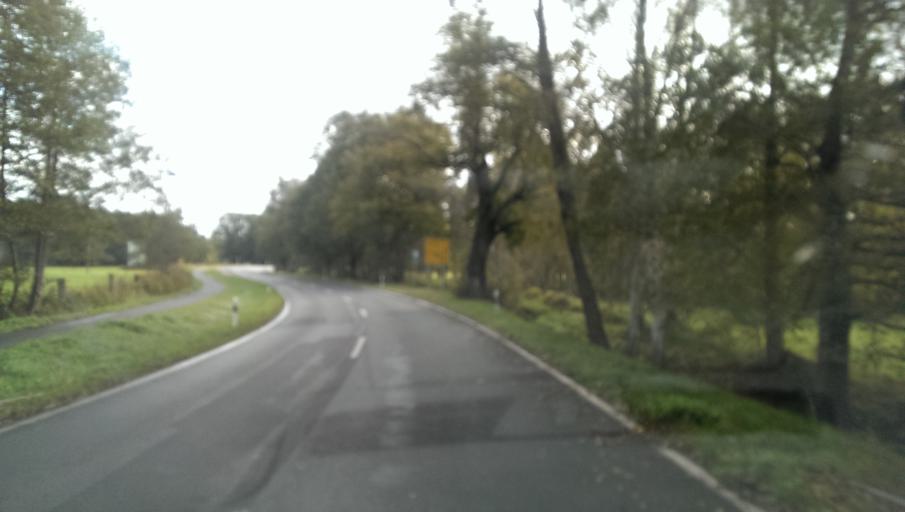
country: DE
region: Brandenburg
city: Luckenwalde
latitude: 52.0623
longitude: 13.1564
